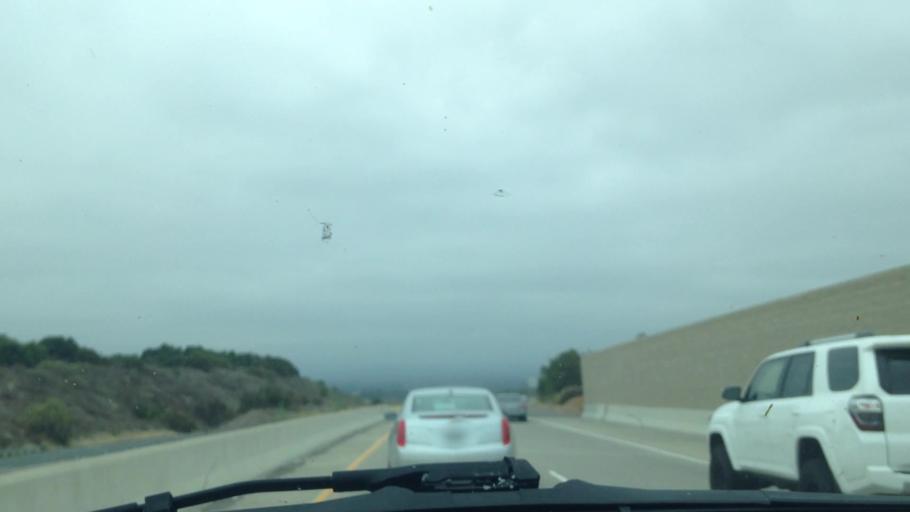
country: US
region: California
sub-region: Orange County
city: North Tustin
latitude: 33.7624
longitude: -117.7597
